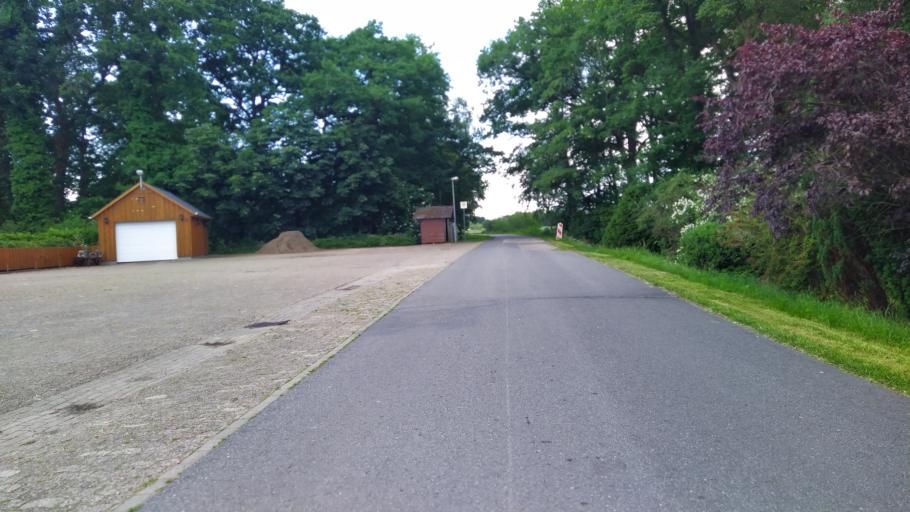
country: DE
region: Lower Saxony
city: Odisheim
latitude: 53.6613
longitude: 8.9311
